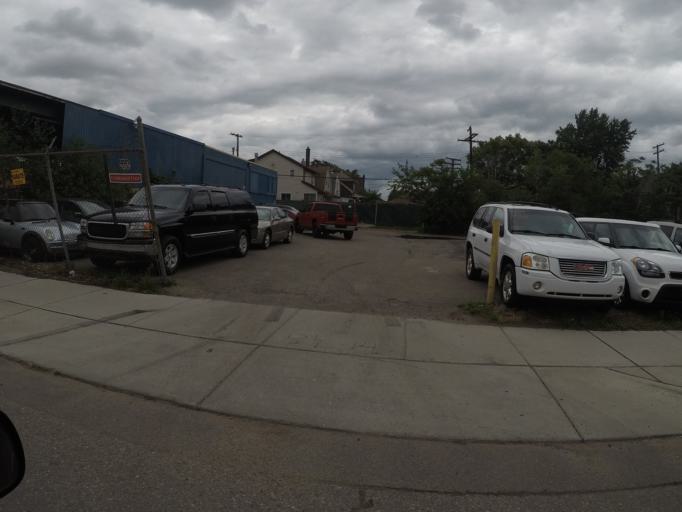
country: US
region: Michigan
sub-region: Wayne County
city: River Rouge
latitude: 42.3101
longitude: -83.1307
